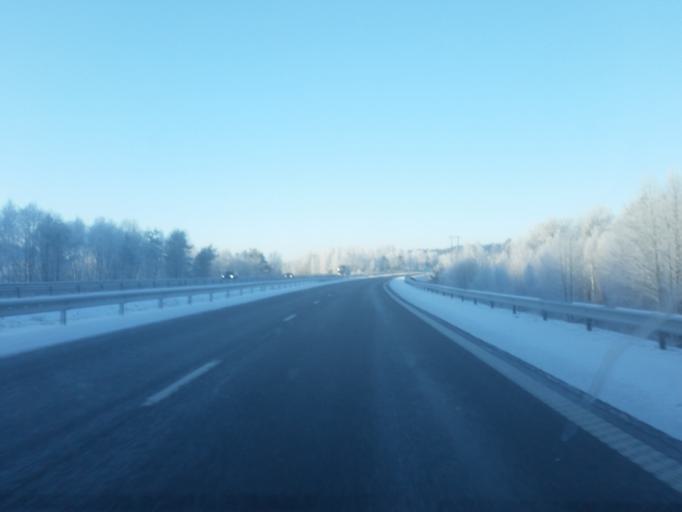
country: SE
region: Vaestra Goetaland
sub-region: Bollebygds Kommun
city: Bollebygd
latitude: 57.6612
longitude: 12.5648
